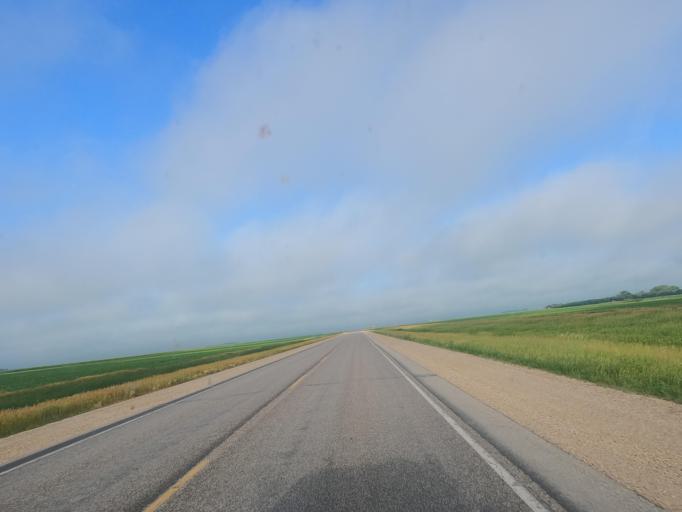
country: CA
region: Manitoba
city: Headingley
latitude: 49.7571
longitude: -97.6649
